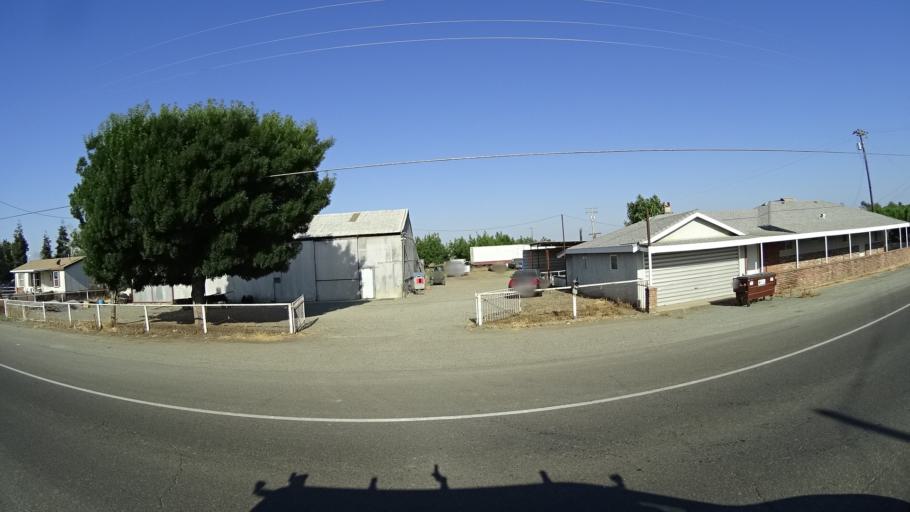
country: US
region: California
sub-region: Kings County
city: Armona
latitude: 36.3386
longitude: -119.7090
